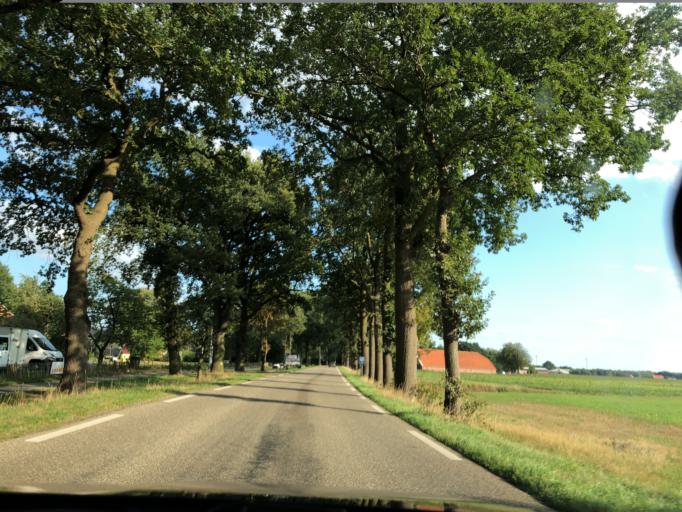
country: NL
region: Groningen
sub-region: Gemeente Vlagtwedde
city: Vlagtwedde
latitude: 53.0216
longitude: 7.1721
